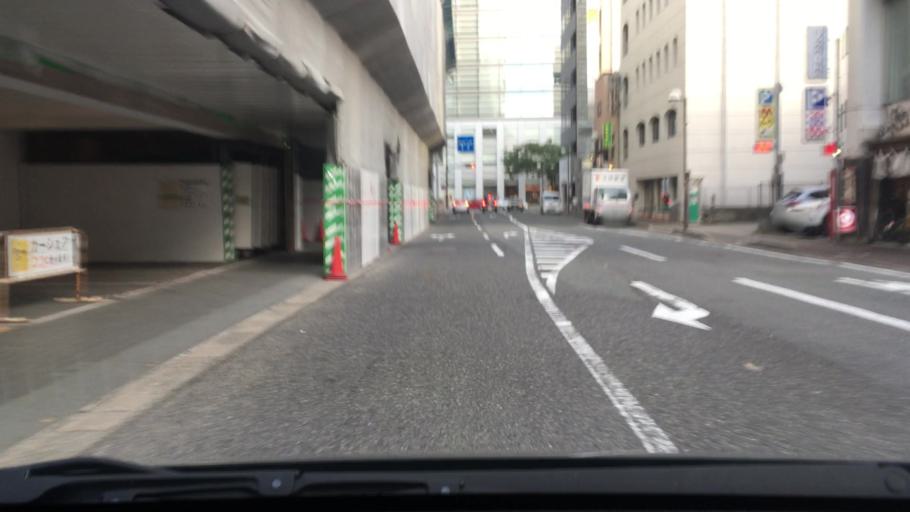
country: JP
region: Fukuoka
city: Fukuoka-shi
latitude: 33.5932
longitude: 130.4021
